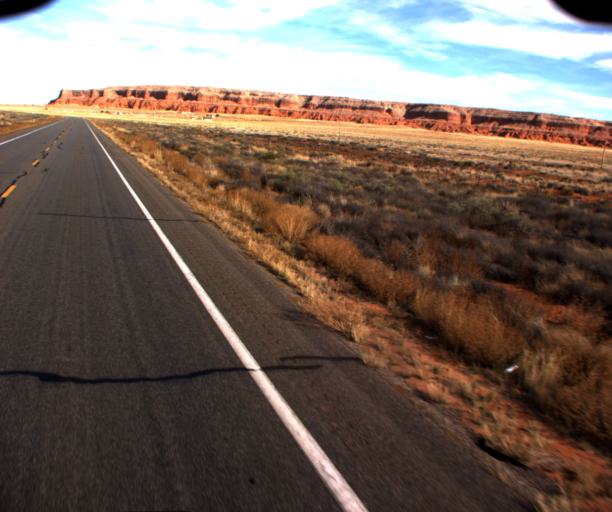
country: US
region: Arizona
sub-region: Navajo County
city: Kayenta
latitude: 36.7857
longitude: -109.9634
